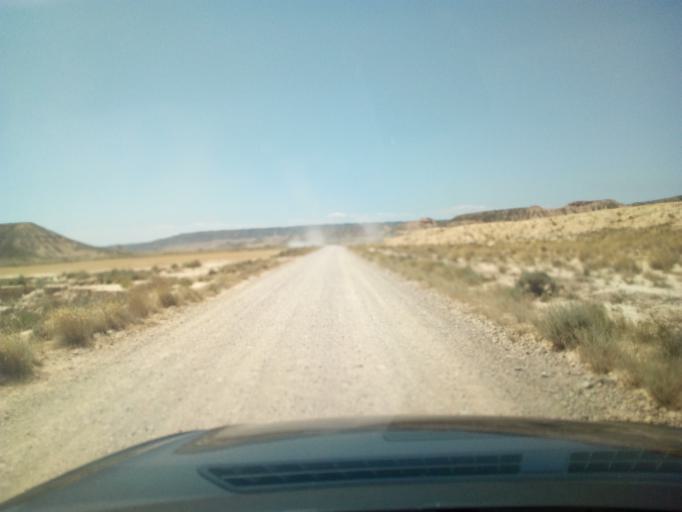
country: ES
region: Navarre
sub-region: Provincia de Navarra
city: Arguedas
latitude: 42.2227
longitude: -1.5002
